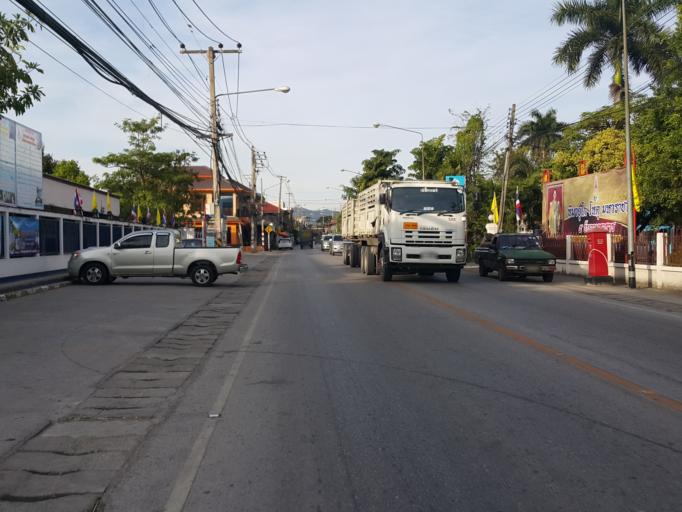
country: TH
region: Chiang Mai
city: San Sai
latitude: 18.8708
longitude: 99.1361
